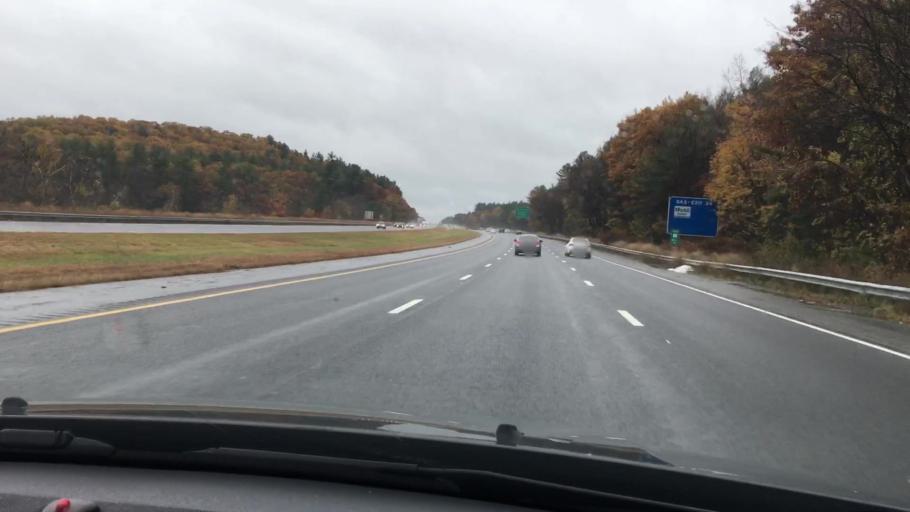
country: US
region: Massachusetts
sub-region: Middlesex County
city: Tyngsboro
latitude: 42.6702
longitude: -71.4376
